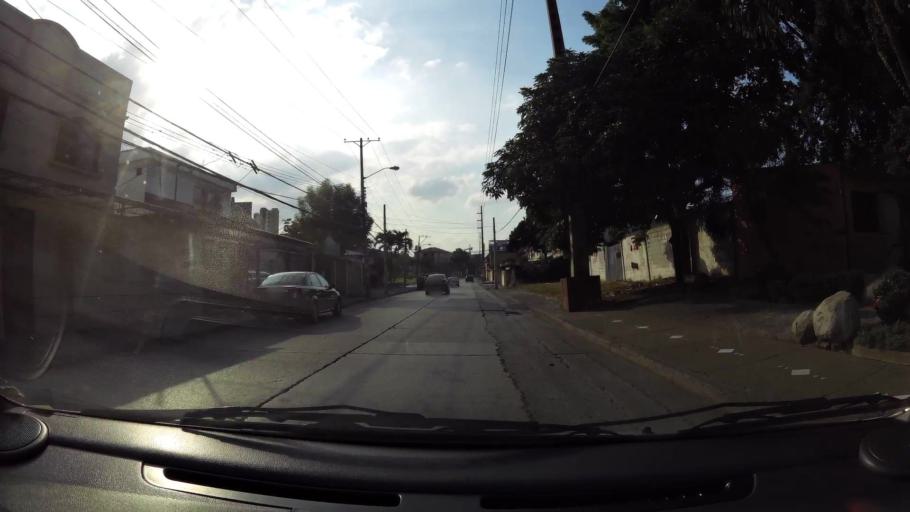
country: EC
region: Guayas
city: Guayaquil
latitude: -2.1556
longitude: -79.9041
